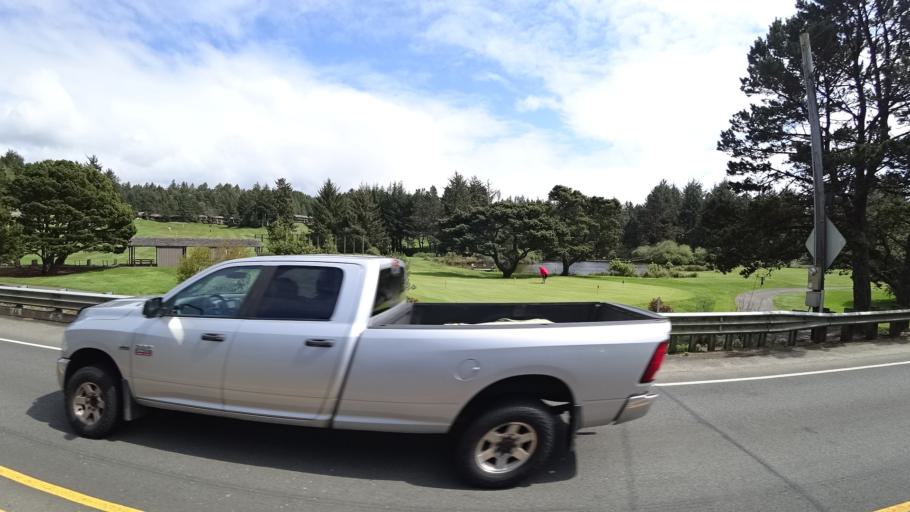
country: US
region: Oregon
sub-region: Lincoln County
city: Lincoln Beach
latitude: 44.8879
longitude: -124.0264
